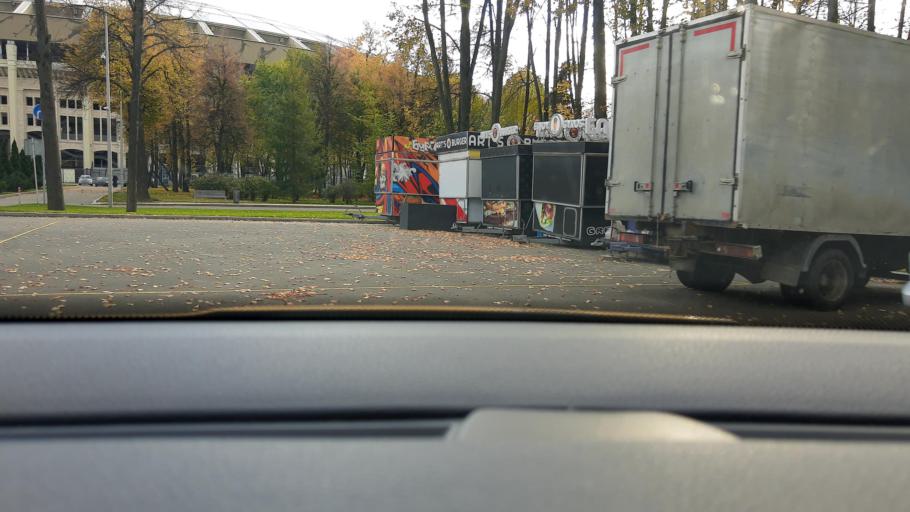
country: RU
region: Moscow
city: Luzhniki
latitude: 55.7185
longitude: 37.5533
